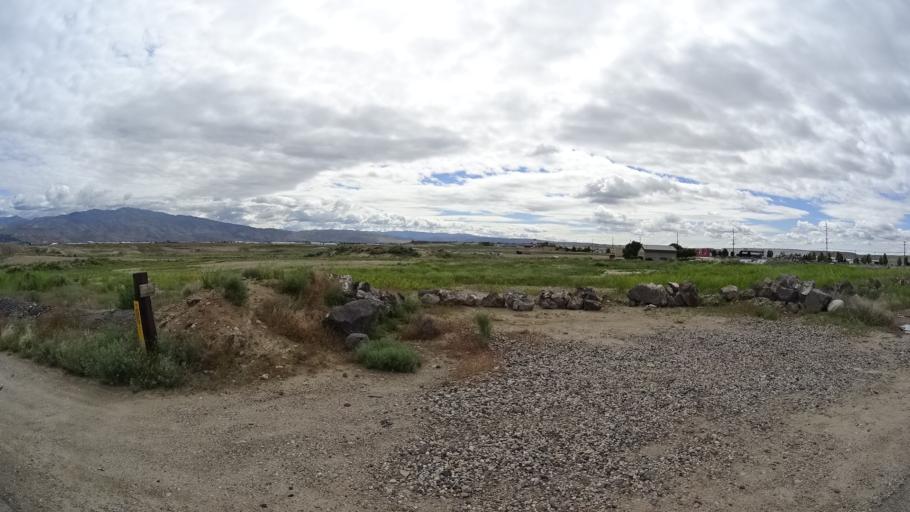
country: US
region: Idaho
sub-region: Ada County
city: Boise
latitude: 43.5487
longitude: -116.1887
